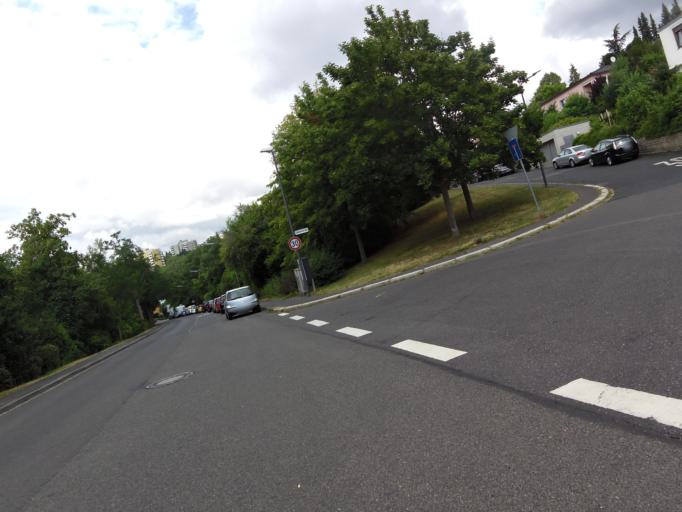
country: DE
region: Bavaria
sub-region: Regierungsbezirk Unterfranken
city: Wuerzburg
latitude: 49.8067
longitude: 9.9646
